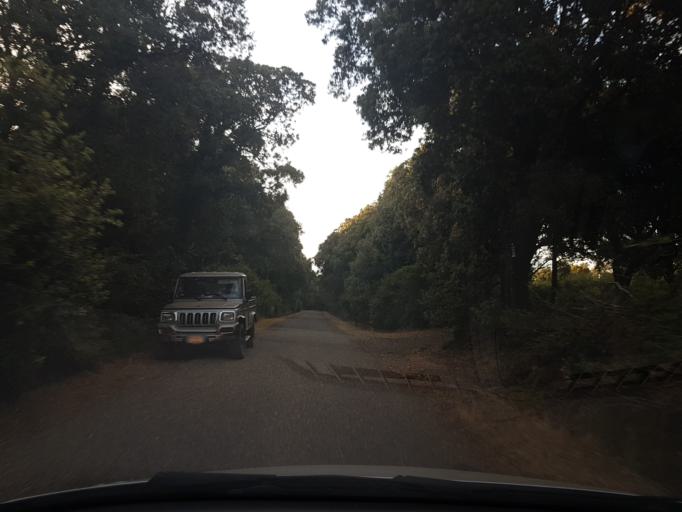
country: IT
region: Sardinia
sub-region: Provincia di Oristano
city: Seneghe
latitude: 40.1089
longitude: 8.5872
